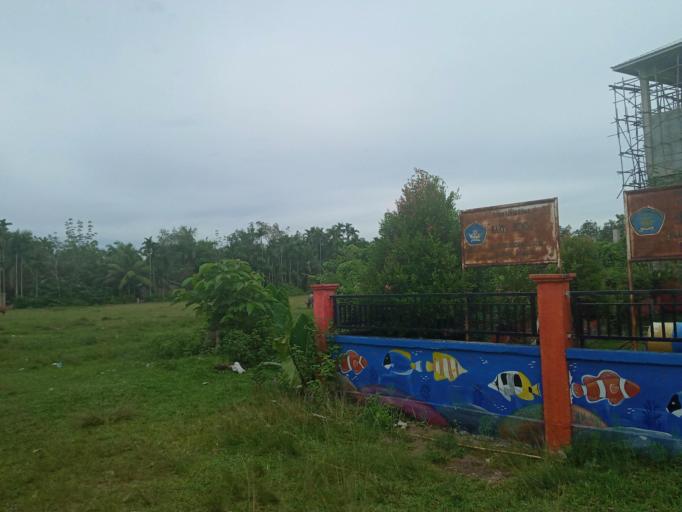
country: ID
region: Jambi
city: Muara Bulian
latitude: -1.6470
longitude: 103.2800
